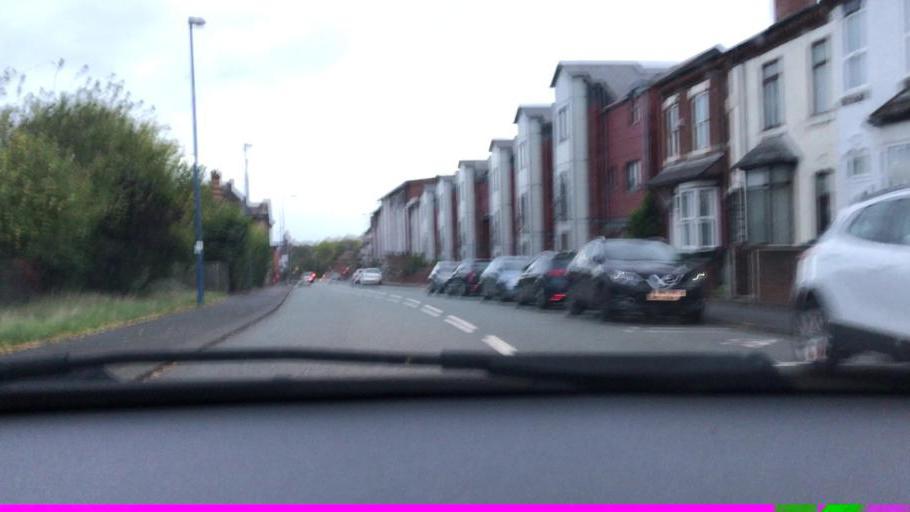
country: GB
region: England
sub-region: Sandwell
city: Smethwick
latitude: 52.4868
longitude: -1.9663
